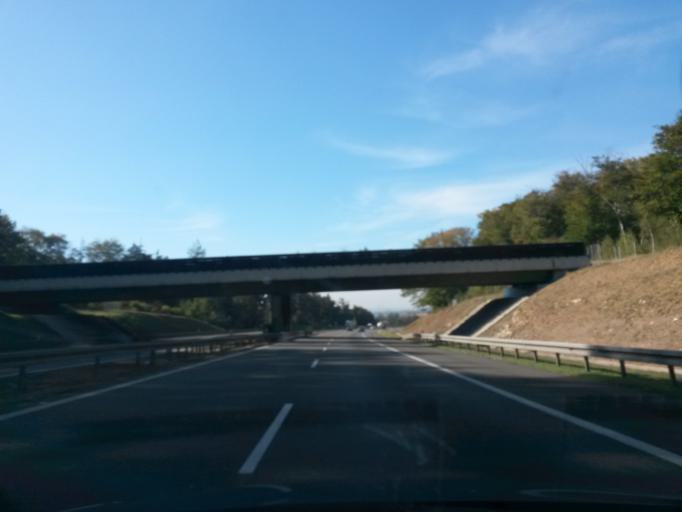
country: PL
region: Opole Voivodeship
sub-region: Powiat krapkowicki
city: Zdzieszowice
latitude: 50.4703
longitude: 18.1442
